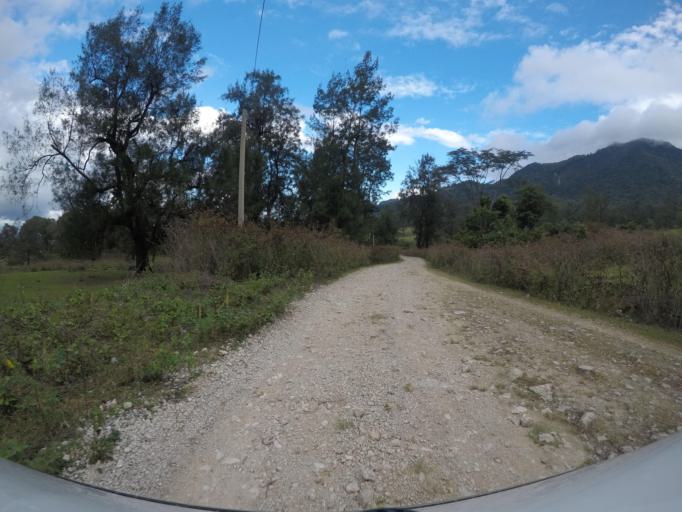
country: TL
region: Baucau
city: Venilale
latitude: -8.6801
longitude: 126.6411
